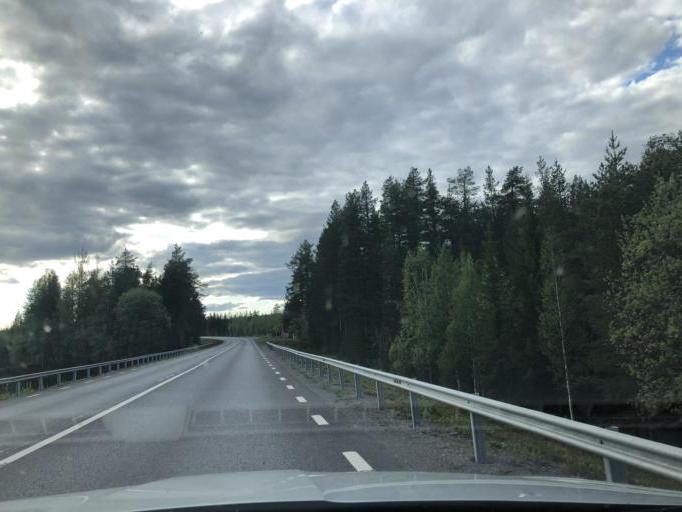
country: SE
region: Norrbotten
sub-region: Arvidsjaurs Kommun
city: Arvidsjaur
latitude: 65.6097
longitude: 19.0779
